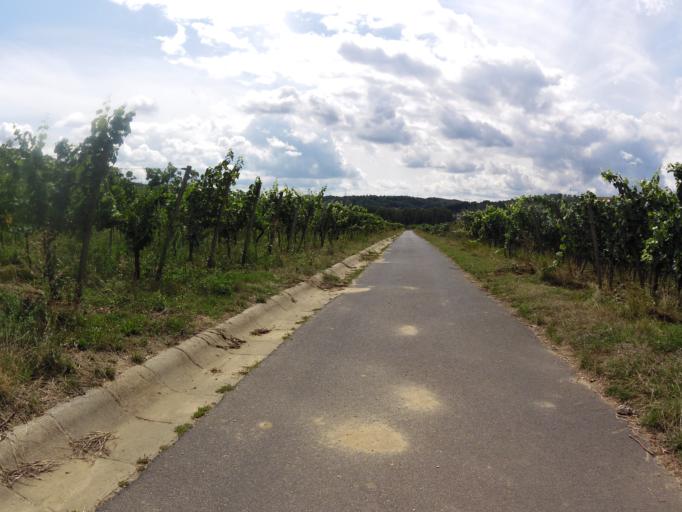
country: DE
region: Bavaria
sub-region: Regierungsbezirk Unterfranken
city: Sommerhausen
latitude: 49.6921
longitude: 10.0289
